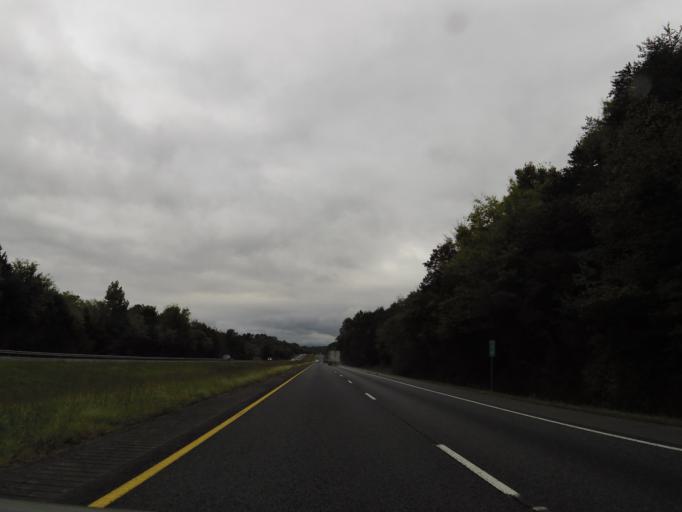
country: US
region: Georgia
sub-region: Dade County
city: Trenton
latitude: 34.9004
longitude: -85.4951
